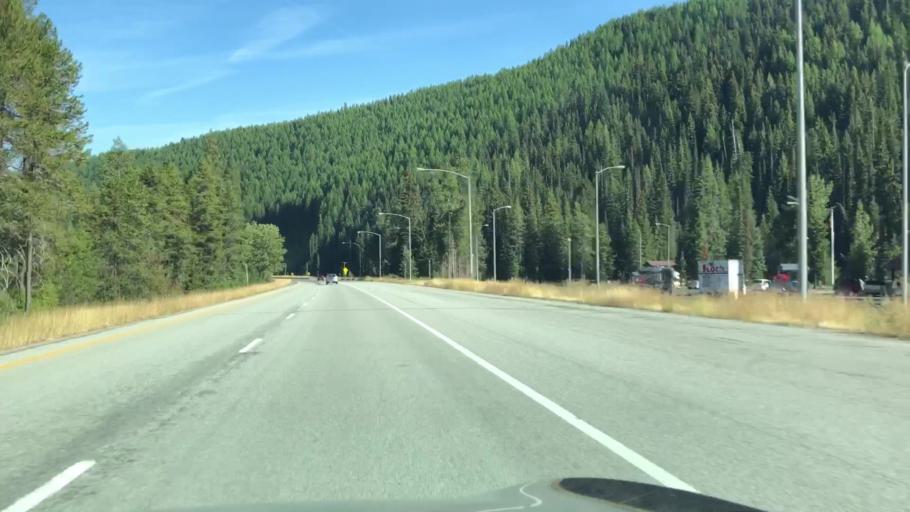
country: US
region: Idaho
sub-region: Shoshone County
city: Wallace
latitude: 47.4204
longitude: -115.6296
